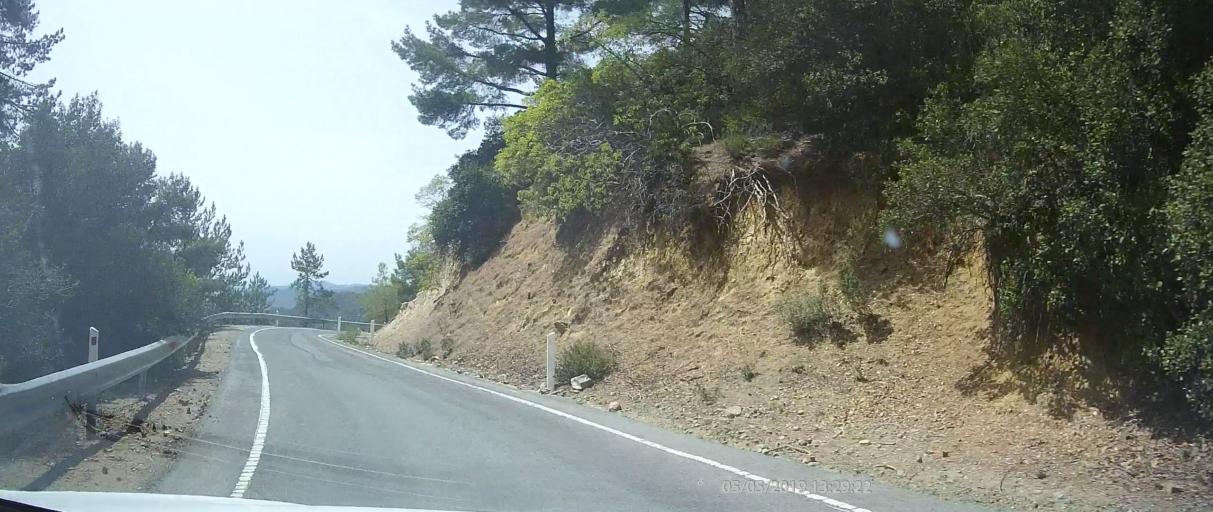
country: CY
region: Lefkosia
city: Kakopetria
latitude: 34.8989
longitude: 32.8500
